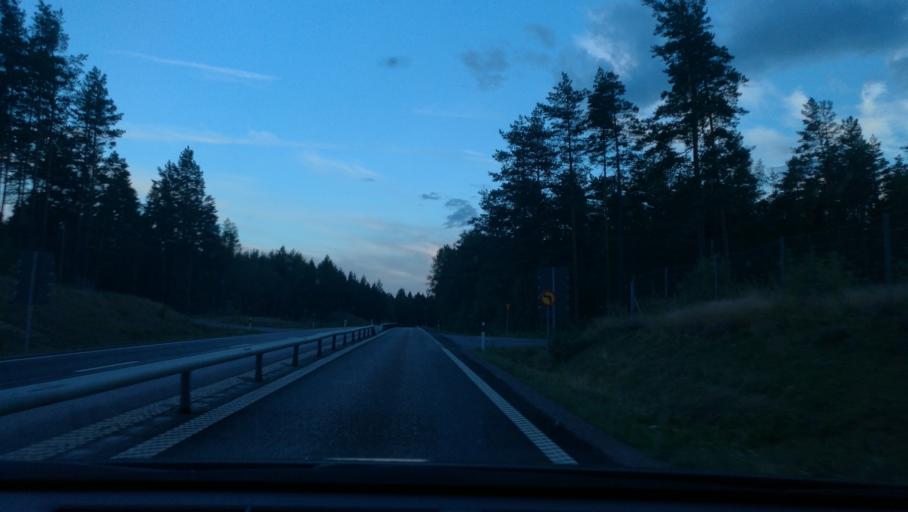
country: SE
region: Soedermanland
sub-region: Katrineholms Kommun
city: Katrineholm
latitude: 58.8620
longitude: 16.2020
